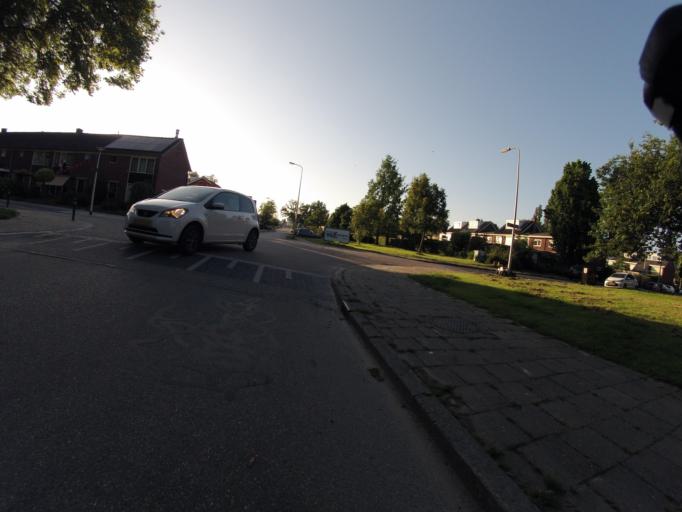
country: NL
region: Overijssel
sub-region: Gemeente Oldenzaal
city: Oldenzaal
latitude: 52.3033
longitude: 6.9377
